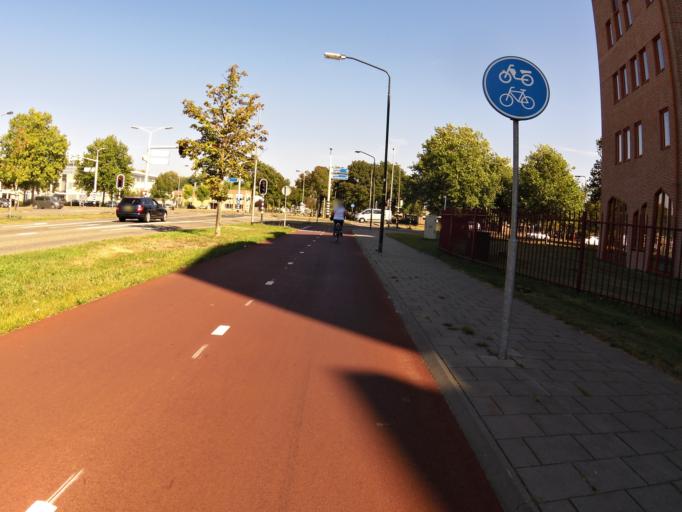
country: NL
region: North Brabant
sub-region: Gemeente Oss
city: Oss
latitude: 51.7587
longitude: 5.5180
